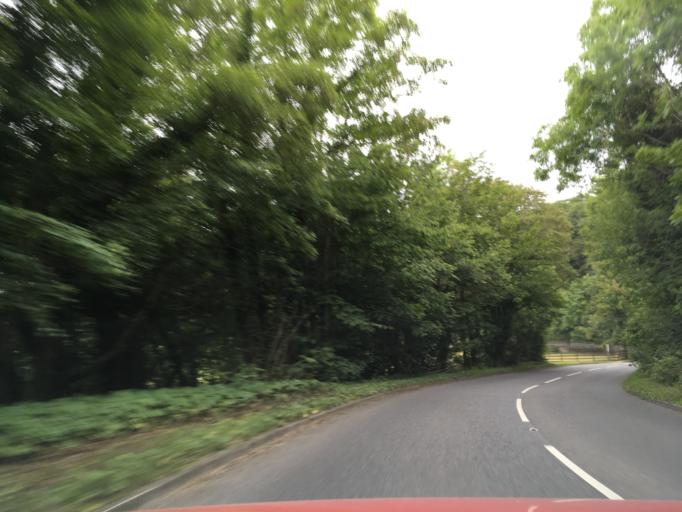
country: GB
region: England
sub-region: North Somerset
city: Long Ashton
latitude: 51.4300
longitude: -2.6960
